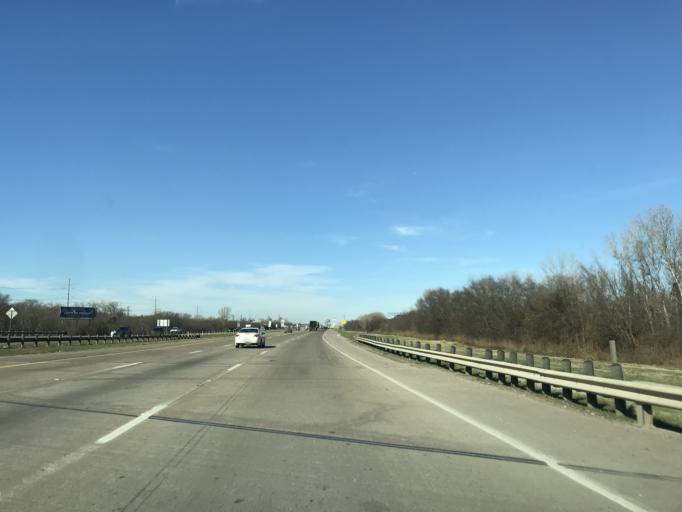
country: US
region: Texas
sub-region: Dallas County
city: Hutchins
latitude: 32.6863
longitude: -96.7473
